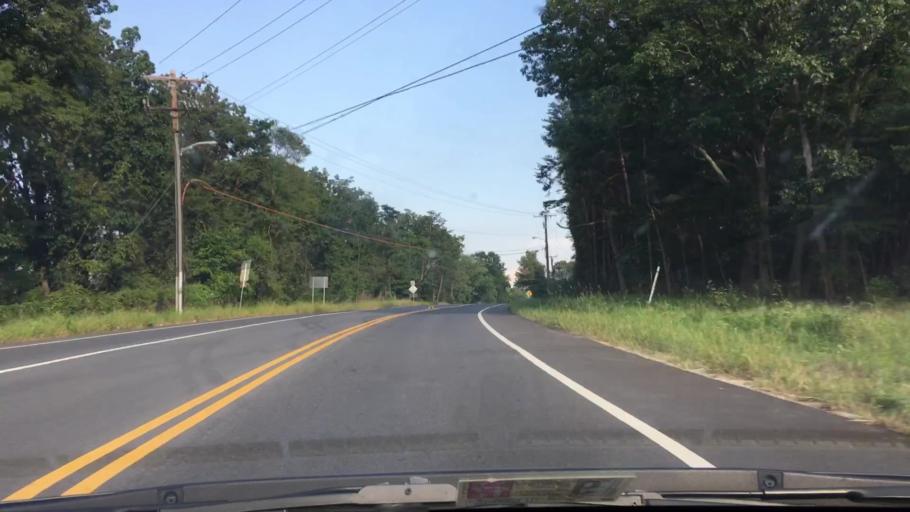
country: US
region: Maryland
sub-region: Prince George's County
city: South Laurel
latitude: 39.0557
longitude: -76.8544
